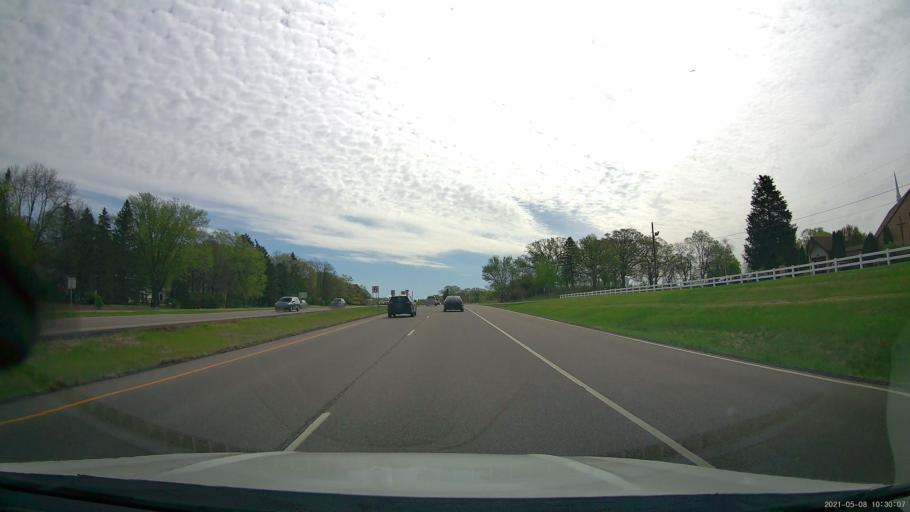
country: US
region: Minnesota
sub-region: Dakota County
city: Mendota Heights
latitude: 44.8841
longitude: -93.1188
